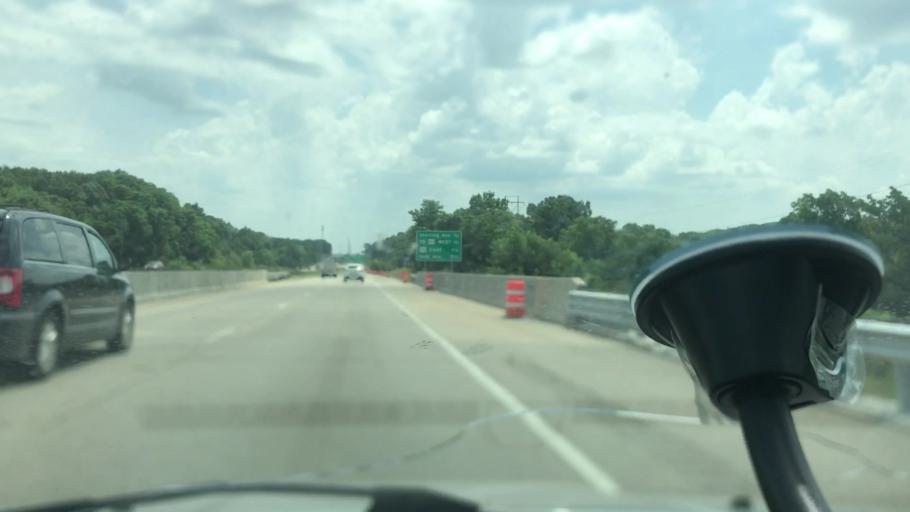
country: US
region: Illinois
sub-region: Peoria County
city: West Peoria
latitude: 40.7401
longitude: -89.6553
